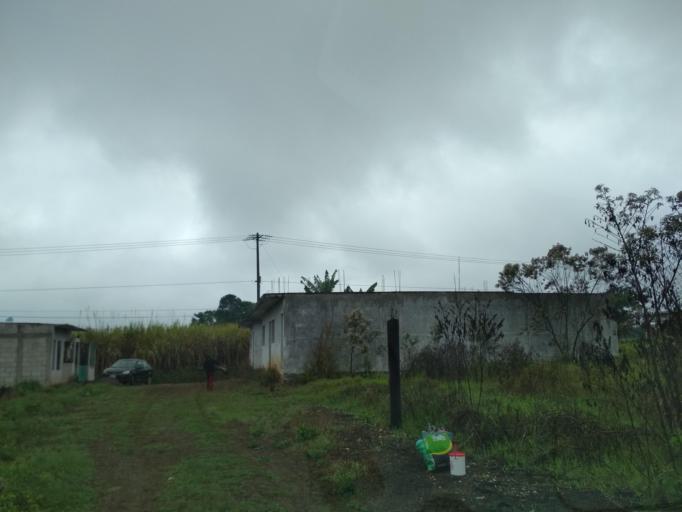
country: MX
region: Veracruz
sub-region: Amatlan de los Reyes
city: Centro de Readaptacion Social
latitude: 18.8350
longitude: -96.9373
